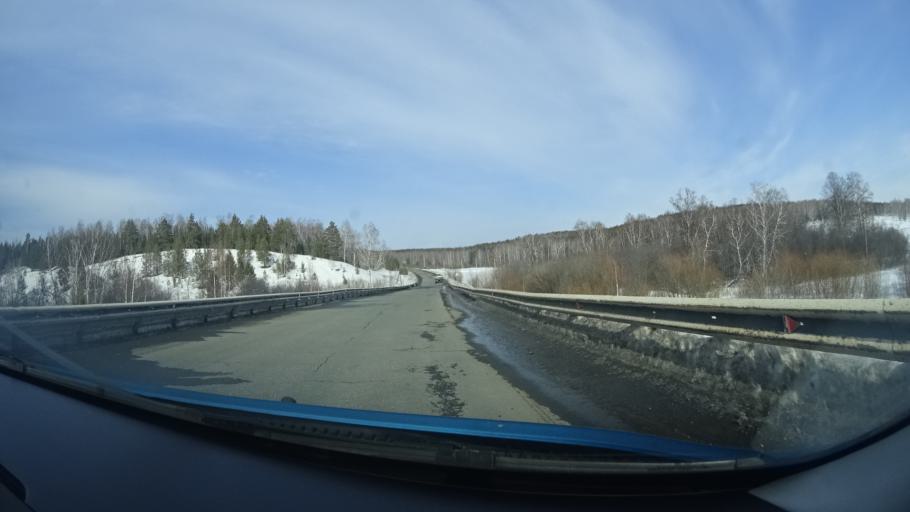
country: RU
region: Bashkortostan
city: Lomovka
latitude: 53.8188
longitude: 58.2766
